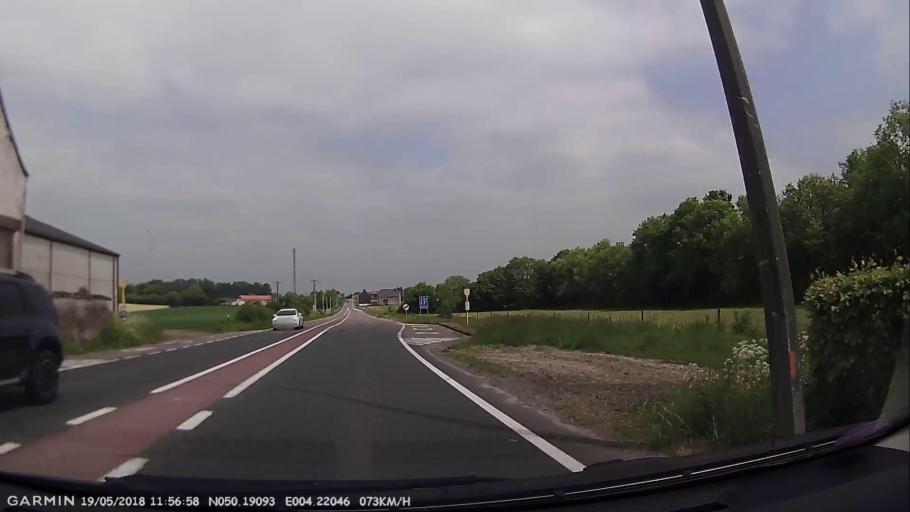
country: BE
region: Wallonia
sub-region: Province du Hainaut
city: Beaumont
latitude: 50.1912
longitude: 4.2206
